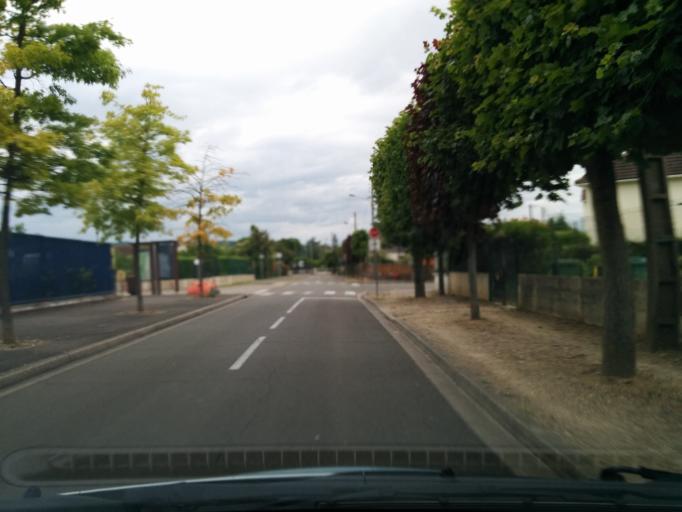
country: FR
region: Ile-de-France
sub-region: Departement des Yvelines
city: Epone
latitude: 48.9707
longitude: 1.8332
